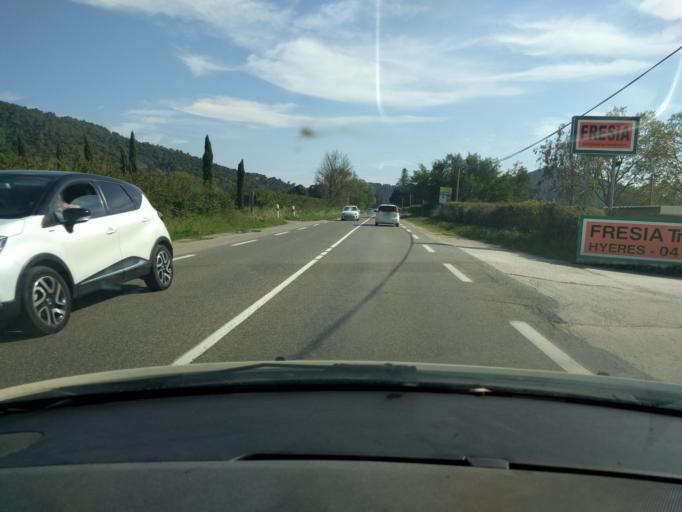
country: FR
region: Provence-Alpes-Cote d'Azur
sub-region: Departement du Var
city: La Crau
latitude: 43.1759
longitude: 6.1178
